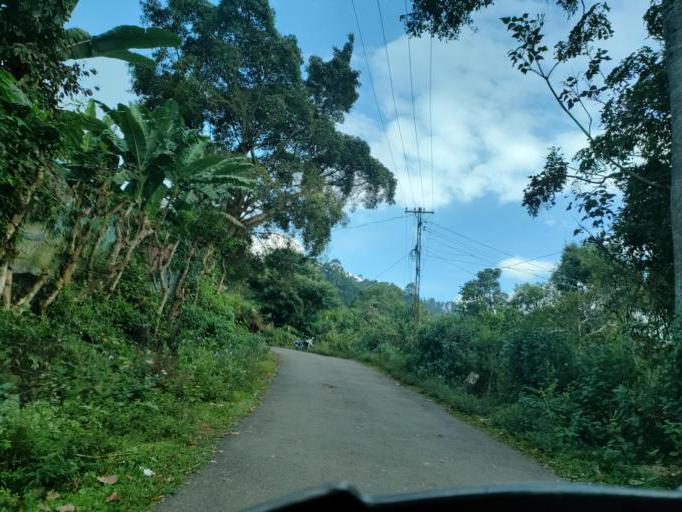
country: IN
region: Tamil Nadu
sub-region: Dindigul
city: Kodaikanal
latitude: 10.2771
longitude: 77.5324
